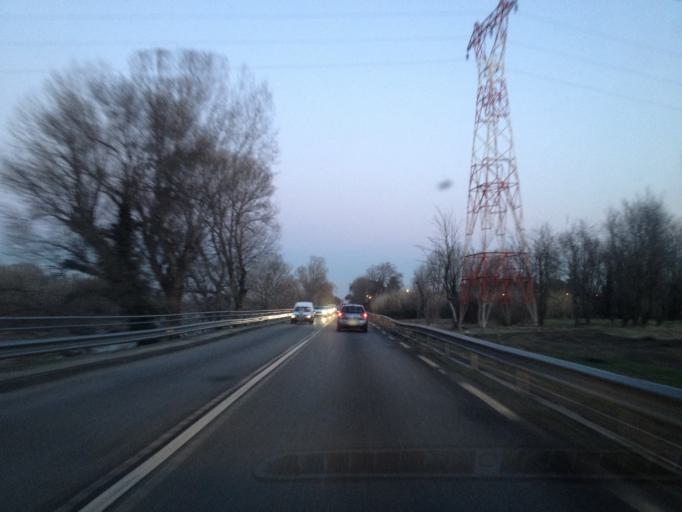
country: FR
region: Provence-Alpes-Cote d'Azur
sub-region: Departement du Vaucluse
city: Avignon
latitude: 43.9590
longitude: 4.8326
